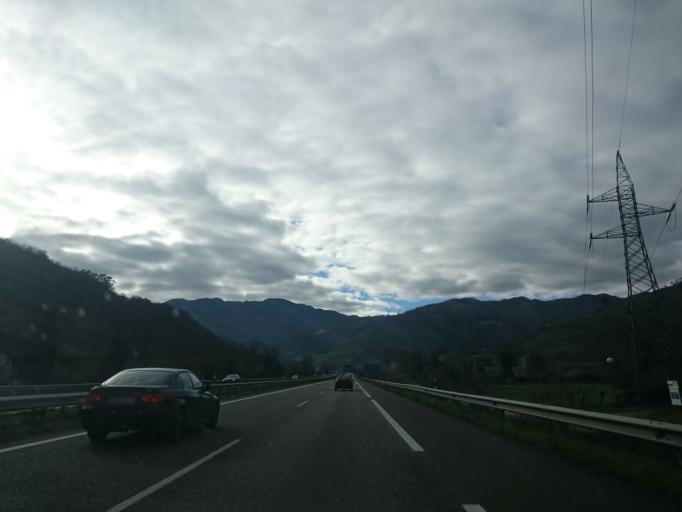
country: ES
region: Asturias
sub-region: Province of Asturias
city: Pola de Lena
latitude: 43.1761
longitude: -5.8170
